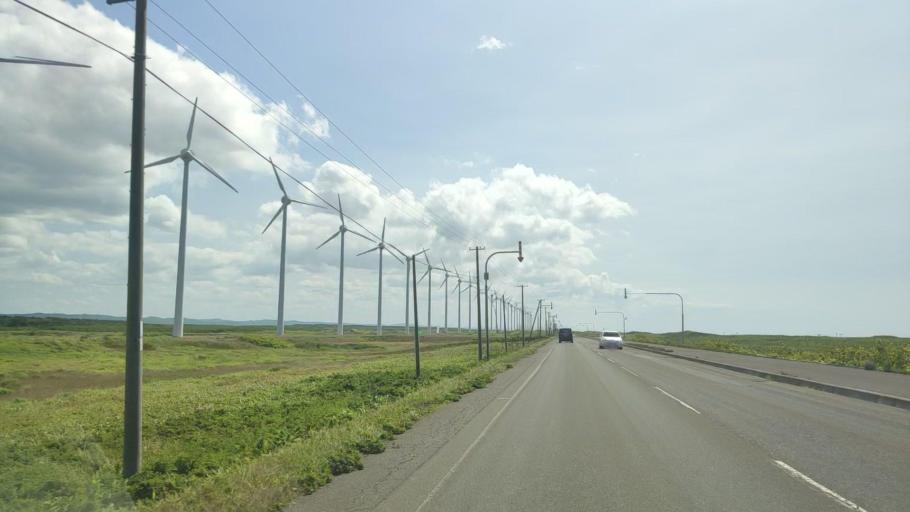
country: JP
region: Hokkaido
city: Makubetsu
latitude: 44.9829
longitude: 141.6922
